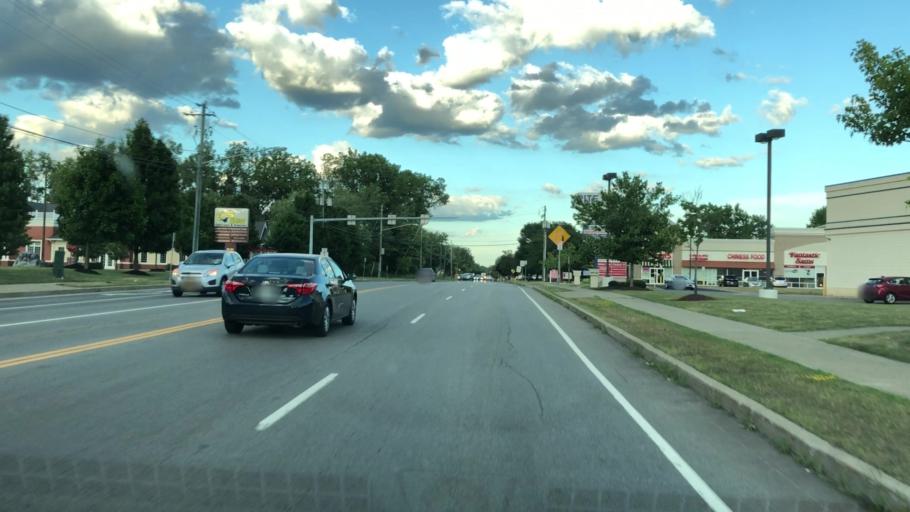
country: US
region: New York
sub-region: Erie County
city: Cheektowaga
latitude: 42.8823
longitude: -78.7536
